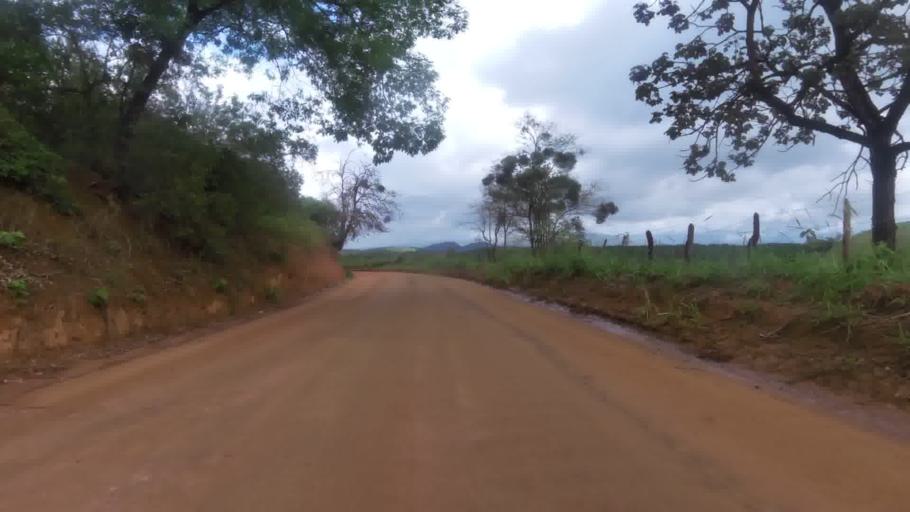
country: BR
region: Espirito Santo
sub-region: Piuma
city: Piuma
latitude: -20.7864
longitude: -40.6317
